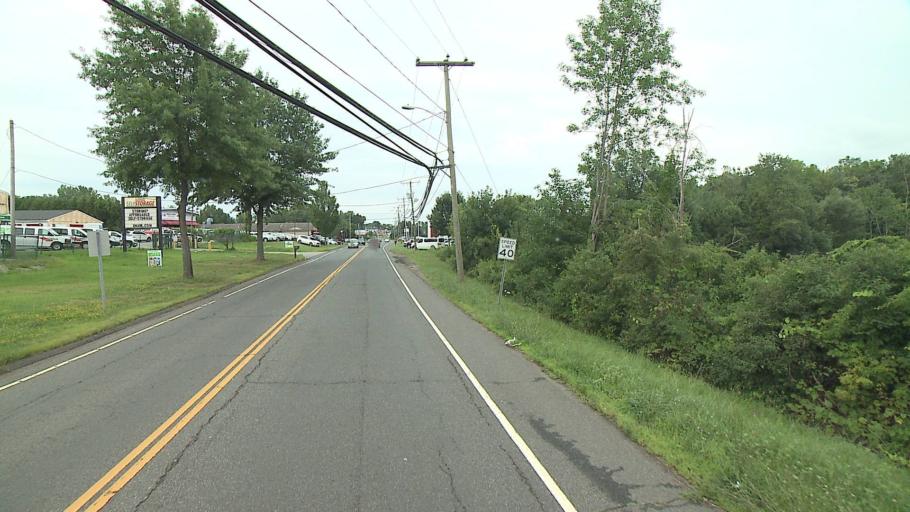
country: US
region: Connecticut
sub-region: Middlesex County
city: Cromwell
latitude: 41.5917
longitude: -72.6760
